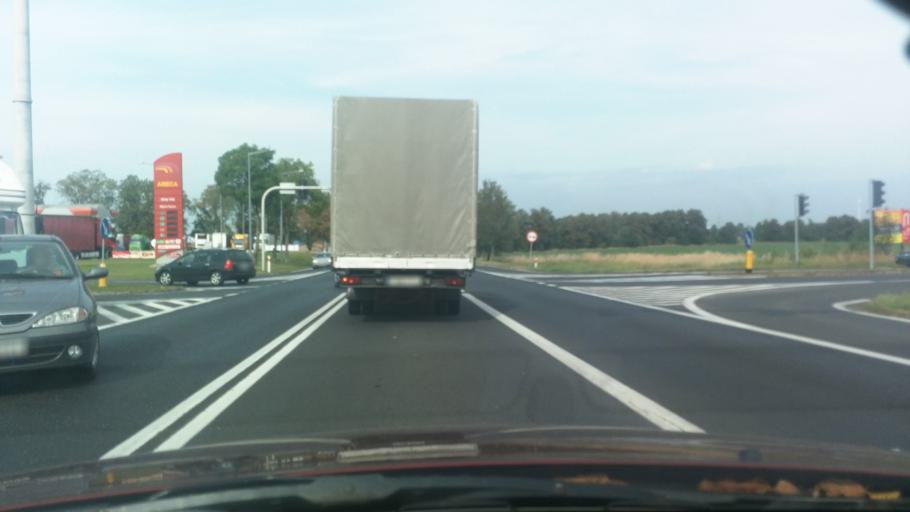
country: PL
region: Lower Silesian Voivodeship
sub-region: Powiat zgorzelecki
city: Lagow
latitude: 51.1597
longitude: 15.0293
